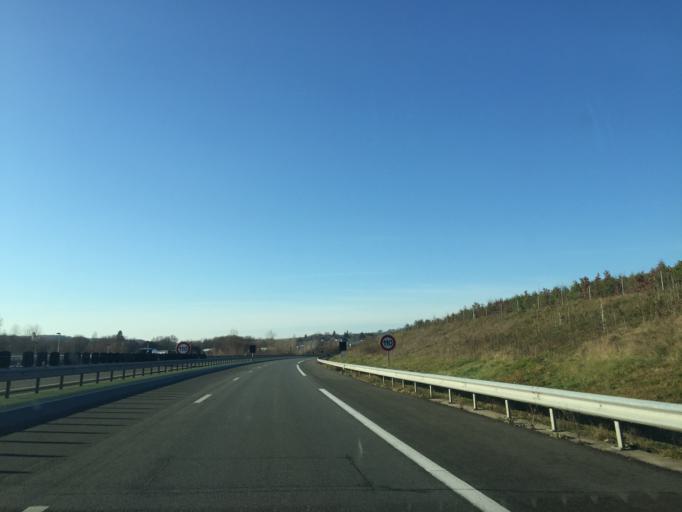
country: FR
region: Aquitaine
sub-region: Departement de la Dordogne
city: Montignac
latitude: 45.1482
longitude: 1.1769
